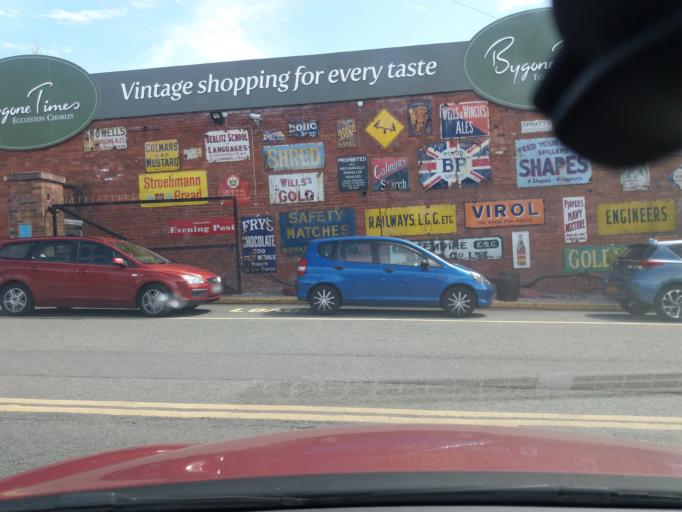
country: GB
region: England
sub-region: Lancashire
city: Euxton
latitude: 53.6416
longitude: -2.7215
